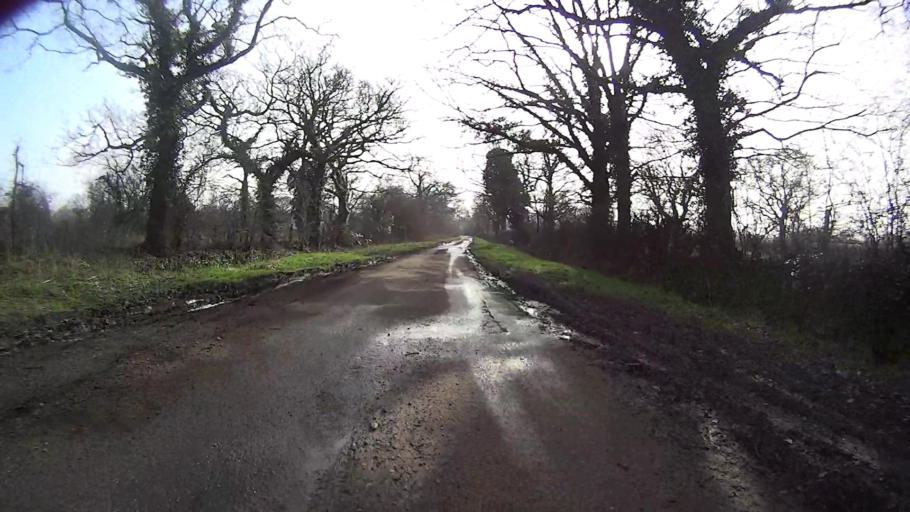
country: GB
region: England
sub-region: West Sussex
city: Copthorne
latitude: 51.1758
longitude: -0.1024
